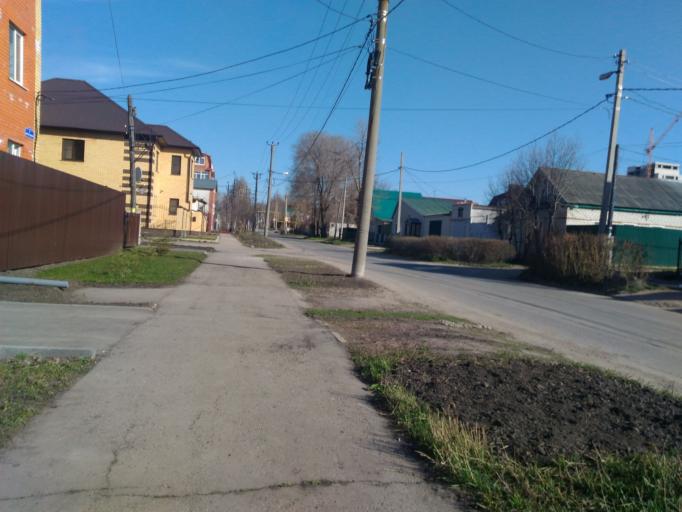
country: RU
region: Ulyanovsk
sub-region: Ulyanovskiy Rayon
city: Ulyanovsk
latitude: 54.3427
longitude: 48.3848
